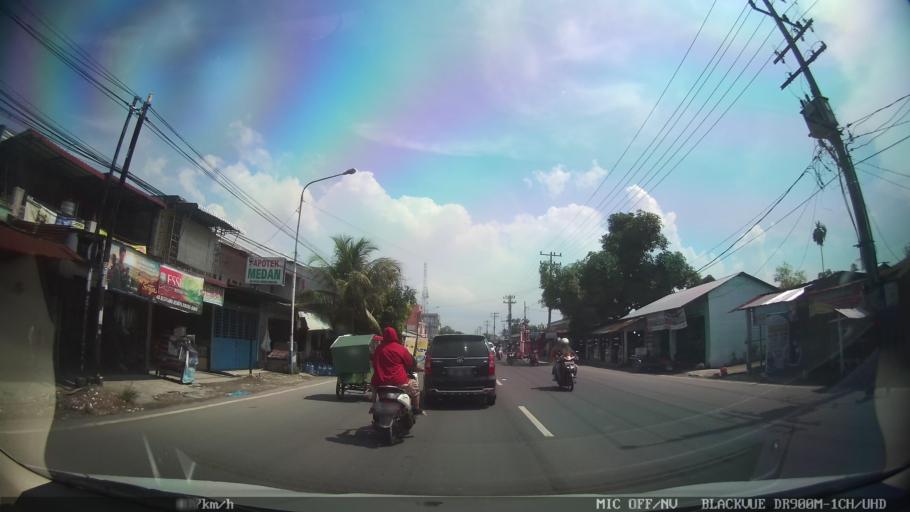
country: ID
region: North Sumatra
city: Medan
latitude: 3.6478
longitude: 98.6574
